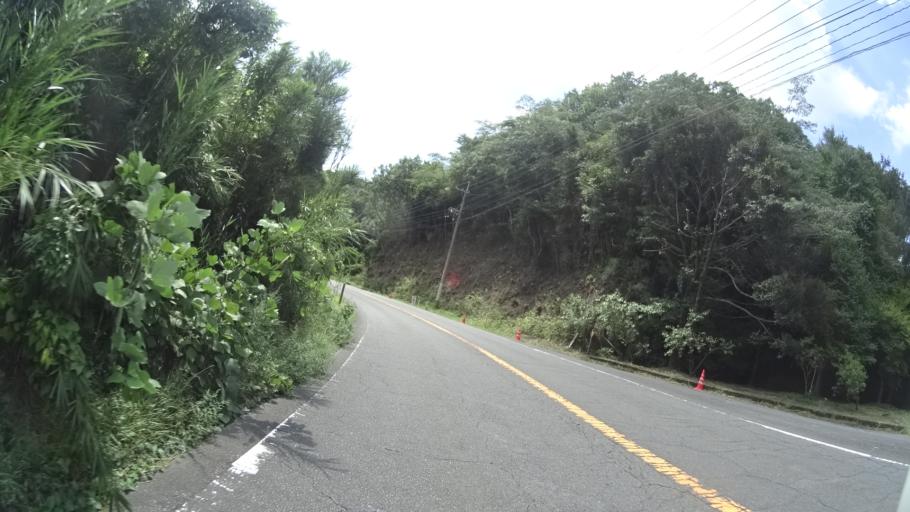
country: JP
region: Kagoshima
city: Kokubu-matsuki
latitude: 31.8723
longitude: 130.7926
